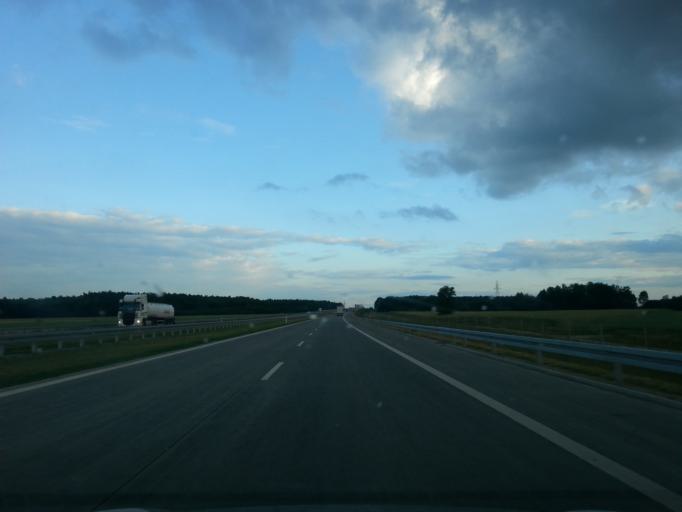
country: PL
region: Lodz Voivodeship
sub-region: Powiat sieradzki
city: Brzeznio
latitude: 51.5170
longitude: 18.6939
